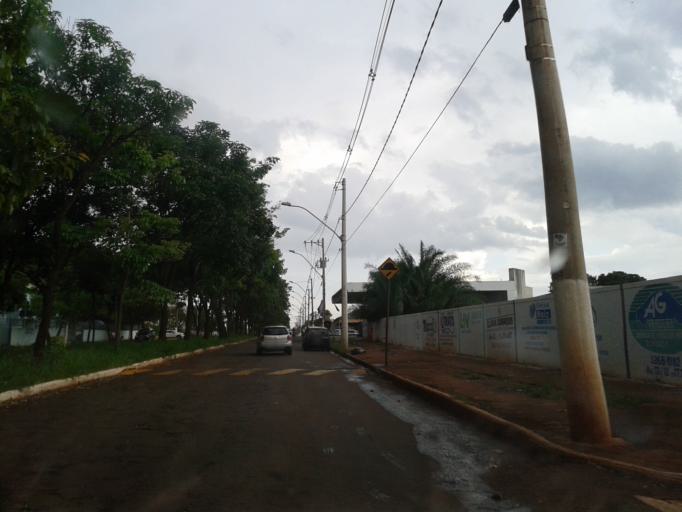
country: BR
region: Minas Gerais
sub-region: Ituiutaba
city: Ituiutaba
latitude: -18.9684
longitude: -49.4747
